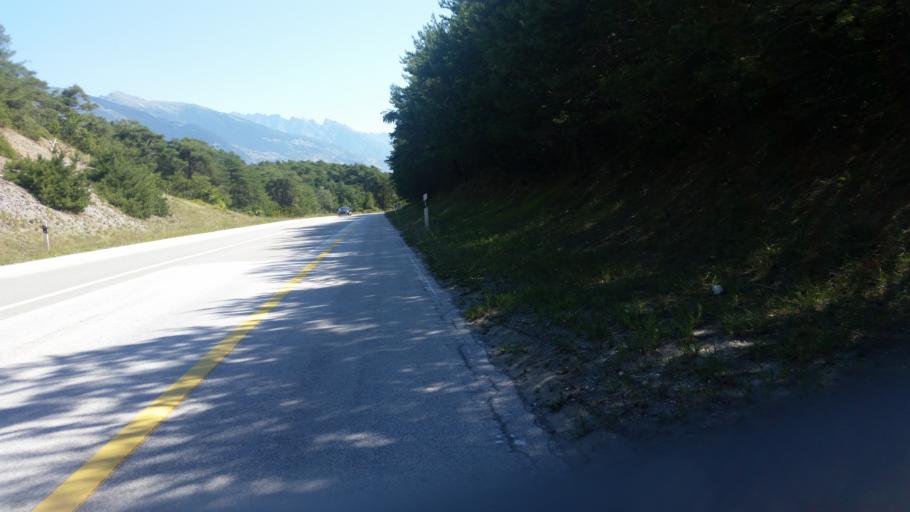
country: CH
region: Valais
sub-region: Leuk District
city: Salgesch
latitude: 46.2933
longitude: 7.5791
